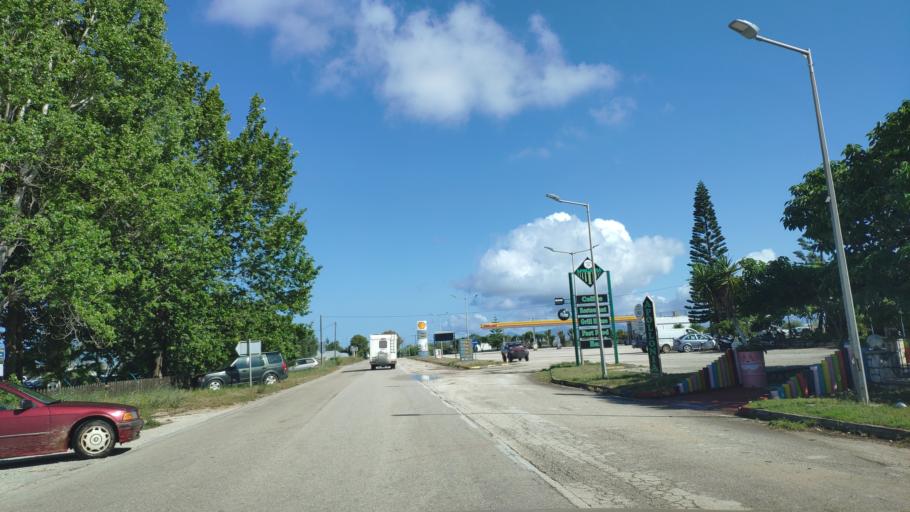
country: GR
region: Epirus
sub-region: Nomos Prevezis
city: Preveza
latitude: 38.9319
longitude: 20.7732
